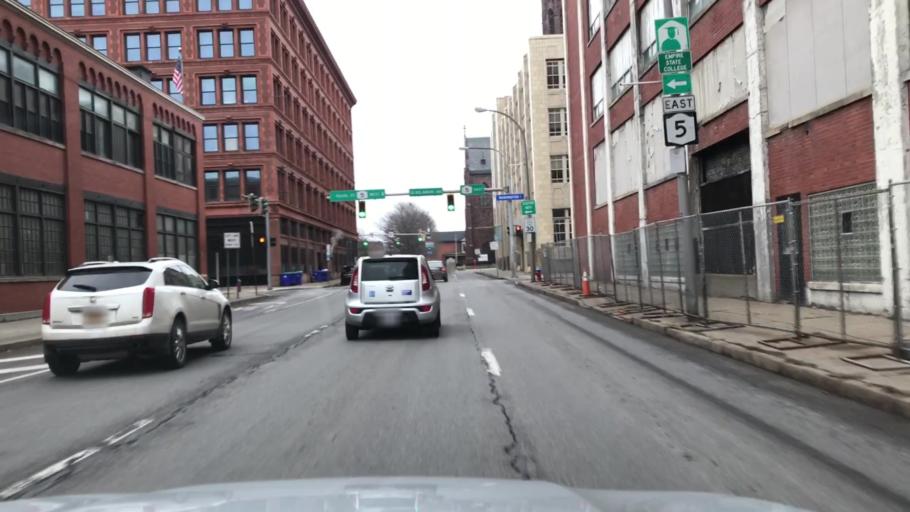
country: US
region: New York
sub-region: Erie County
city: Buffalo
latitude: 42.8951
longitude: -78.8696
